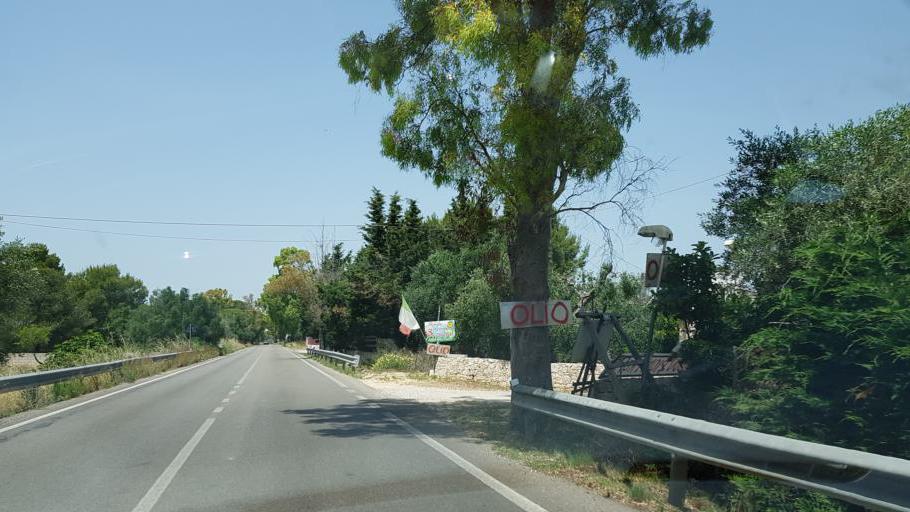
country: IT
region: Apulia
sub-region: Provincia di Lecce
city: Porto Cesareo
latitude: 40.2591
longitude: 17.9235
